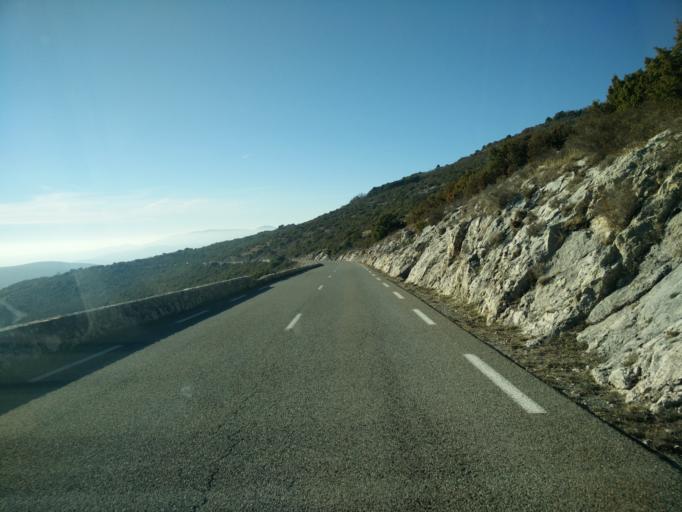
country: FR
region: Provence-Alpes-Cote d'Azur
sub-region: Departement des Alpes-Maritimes
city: Saint-Vallier-de-Thiey
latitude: 43.7084
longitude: 6.8275
